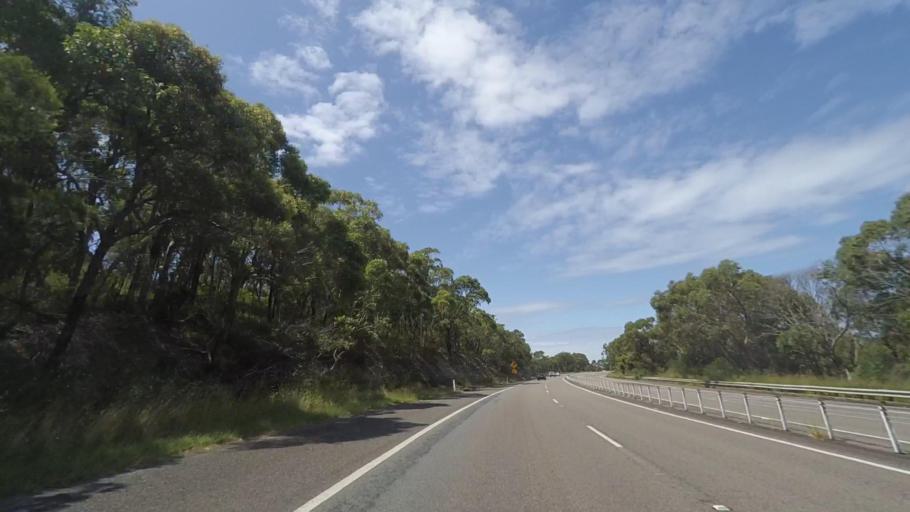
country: AU
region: New South Wales
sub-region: Wyong Shire
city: Kingfisher Shores
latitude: -33.1368
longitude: 151.6095
